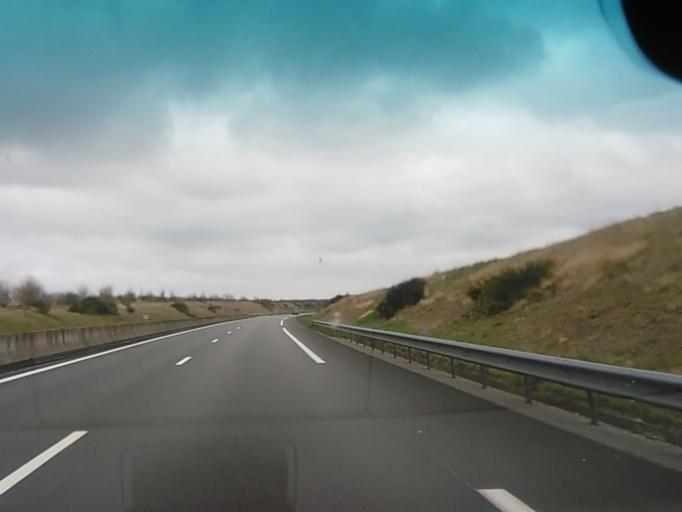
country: FR
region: Lower Normandy
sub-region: Departement du Calvados
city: Orbec
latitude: 48.9456
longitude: 0.4159
